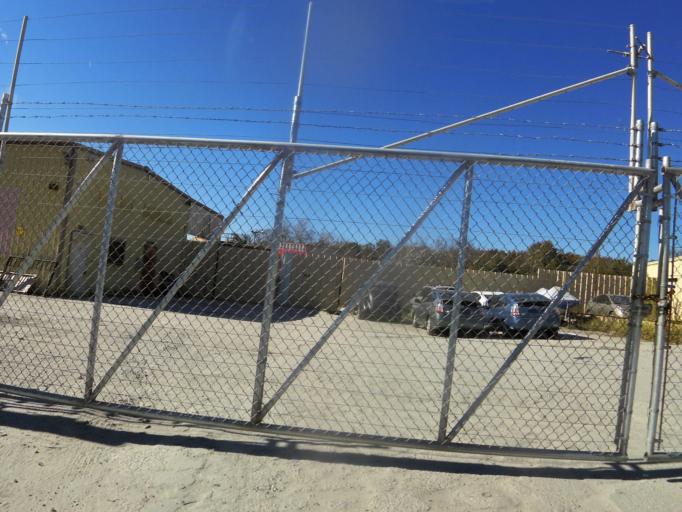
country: US
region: Georgia
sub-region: Chatham County
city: Savannah
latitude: 32.0769
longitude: -81.1170
